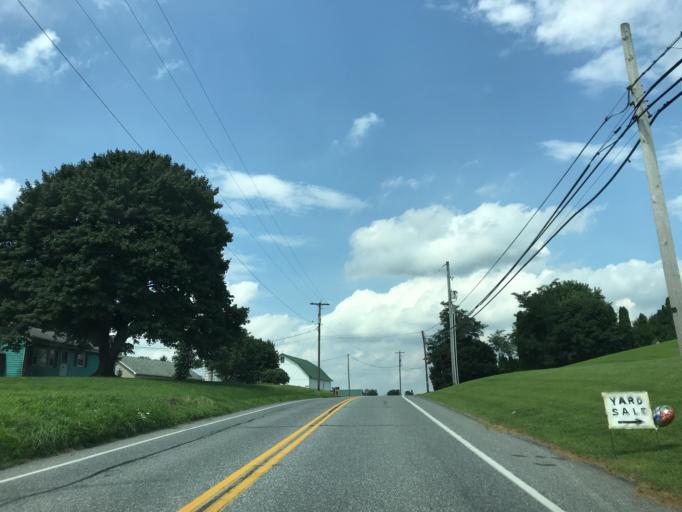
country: US
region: Pennsylvania
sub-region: York County
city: Red Lion
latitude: 39.8538
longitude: -76.6211
